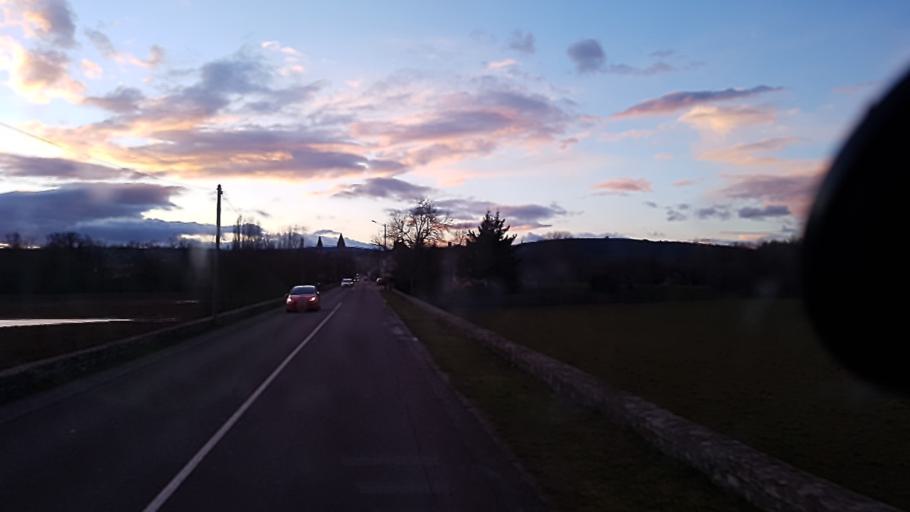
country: FR
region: Bourgogne
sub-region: Departement de Saone-et-Loire
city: Tournus
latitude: 46.5627
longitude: 4.9212
